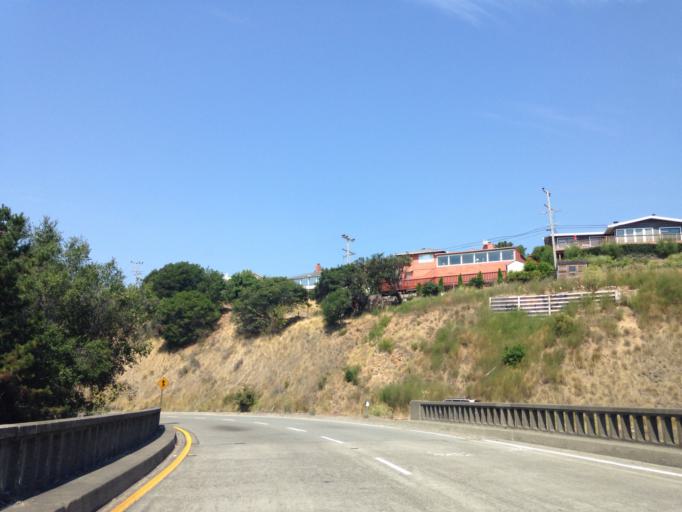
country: US
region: California
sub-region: Marin County
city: Larkspur
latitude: 37.9447
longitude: -122.5153
